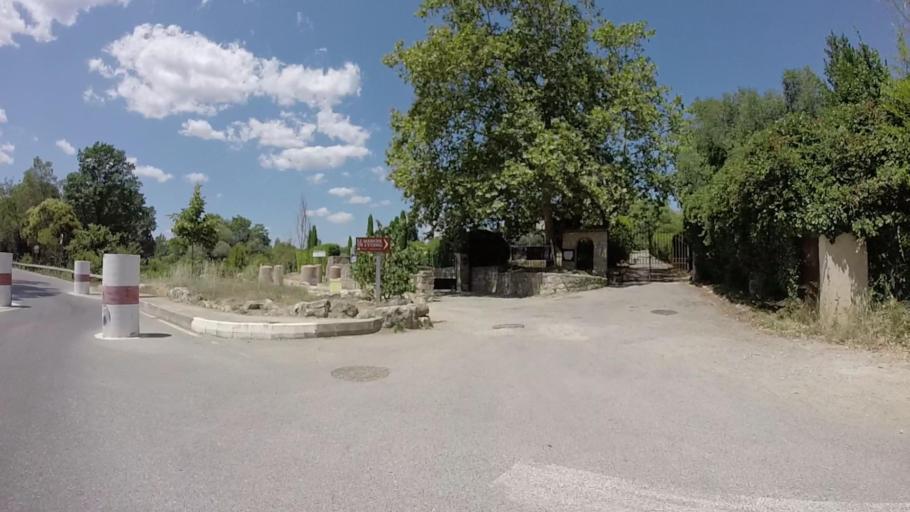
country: FR
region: Provence-Alpes-Cote d'Azur
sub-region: Departement des Alpes-Maritimes
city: Mougins
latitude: 43.5990
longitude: 7.0155
